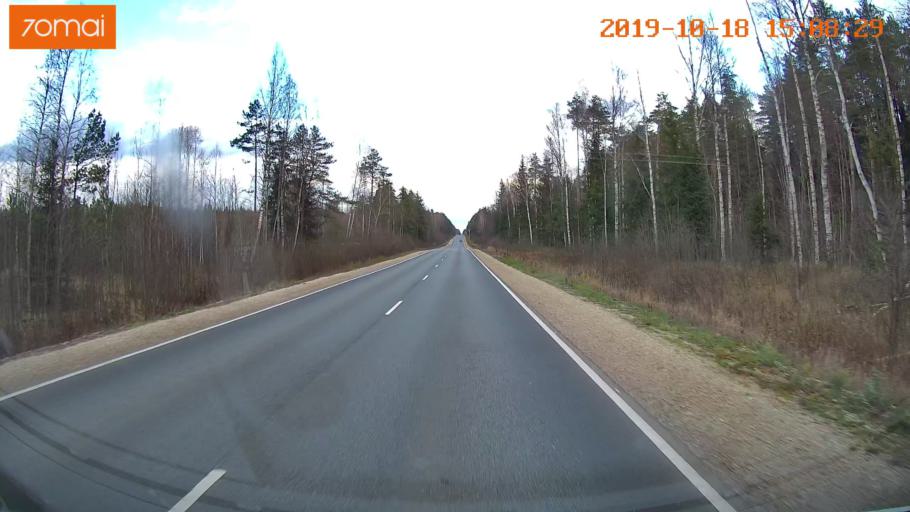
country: RU
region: Vladimir
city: Gus'-Khrustal'nyy
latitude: 55.5531
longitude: 40.6111
